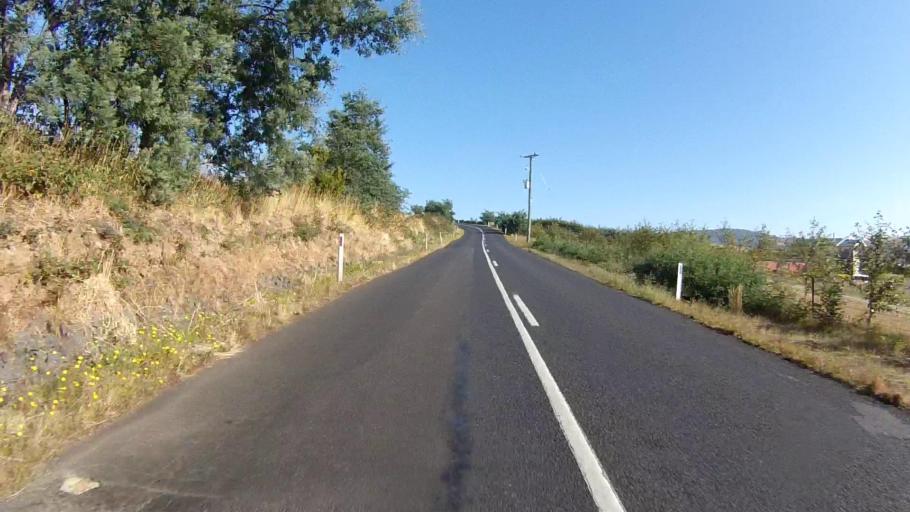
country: AU
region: Tasmania
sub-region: Derwent Valley
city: New Norfolk
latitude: -42.7559
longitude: 146.9854
